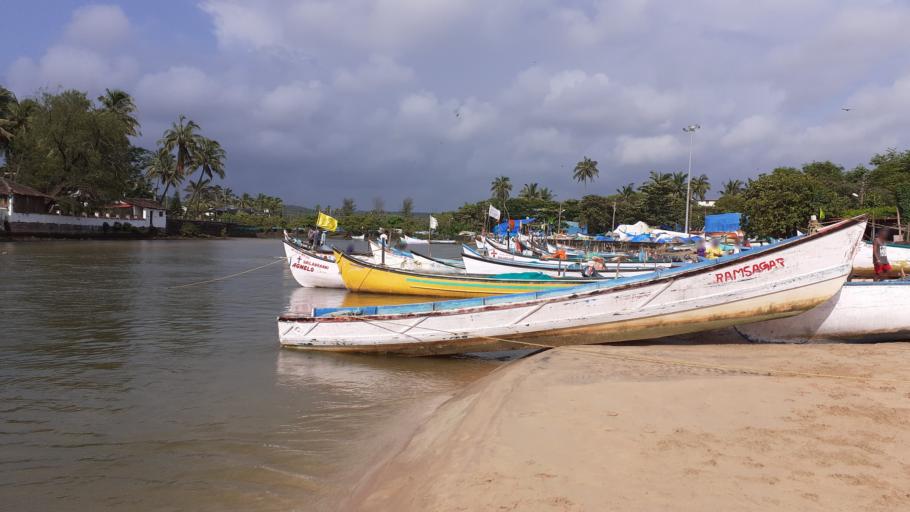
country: IN
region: Goa
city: Calangute
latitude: 15.5631
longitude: 73.7486
